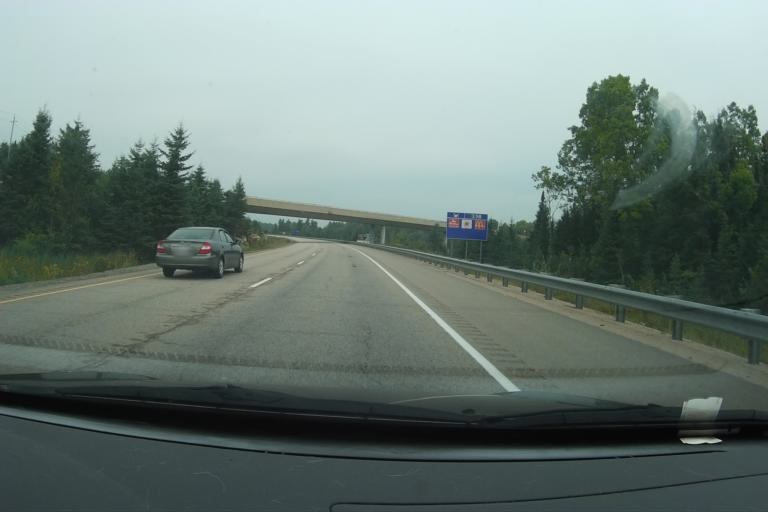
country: CA
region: Ontario
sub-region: Nipissing District
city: North Bay
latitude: 46.2360
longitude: -79.3499
